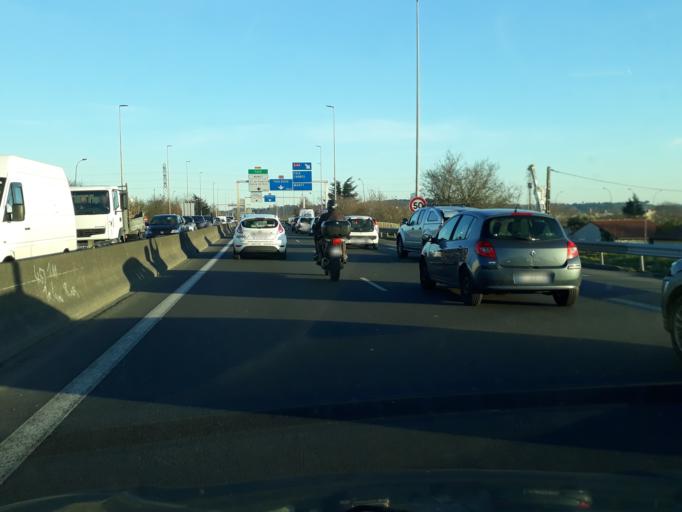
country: FR
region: Midi-Pyrenees
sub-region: Departement de la Haute-Garonne
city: Portet-sur-Garonne
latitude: 43.5559
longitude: 1.4077
